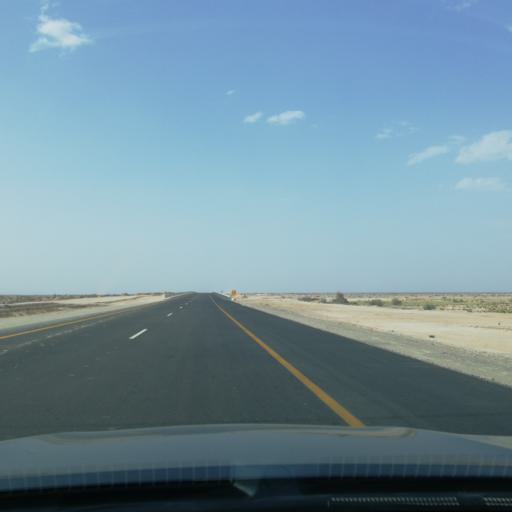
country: OM
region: Muhafazat ad Dakhiliyah
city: Adam
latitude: 22.0883
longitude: 57.5174
